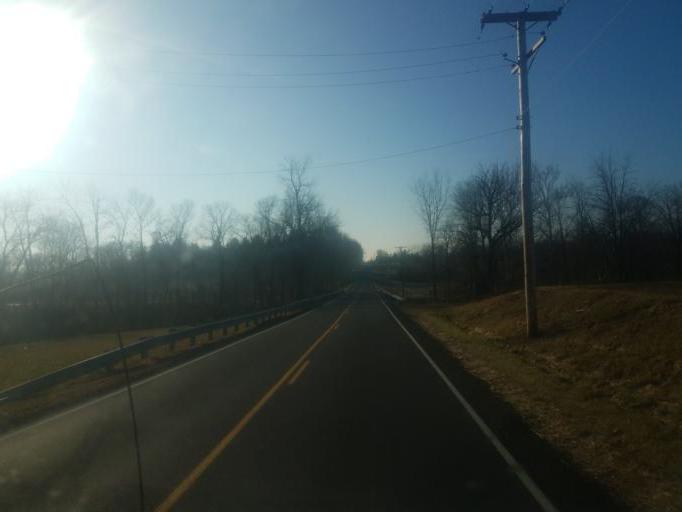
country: US
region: Ohio
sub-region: Crawford County
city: Bucyrus
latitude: 40.8272
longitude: -82.9402
